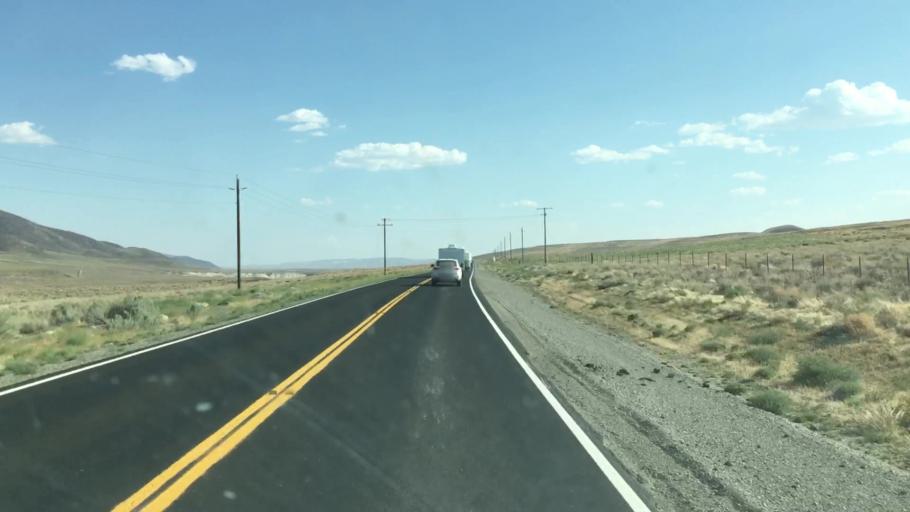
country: US
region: Nevada
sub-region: Lyon County
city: Fernley
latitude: 39.7710
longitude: -119.3445
